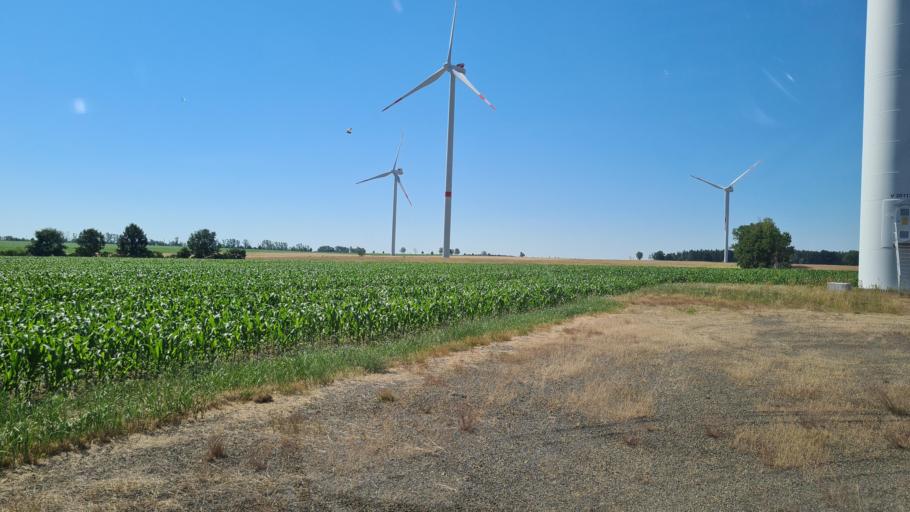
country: DE
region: Brandenburg
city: Niedergorsdorf
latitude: 52.0121
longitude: 12.9051
